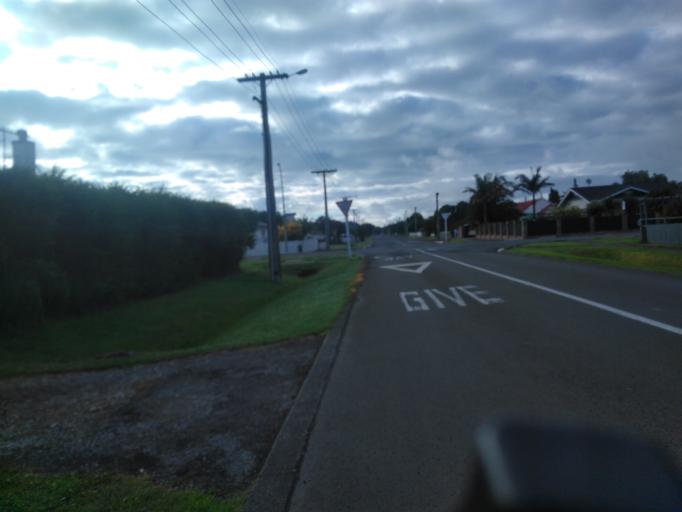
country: NZ
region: Gisborne
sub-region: Gisborne District
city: Gisborne
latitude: -38.6539
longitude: 178.0260
